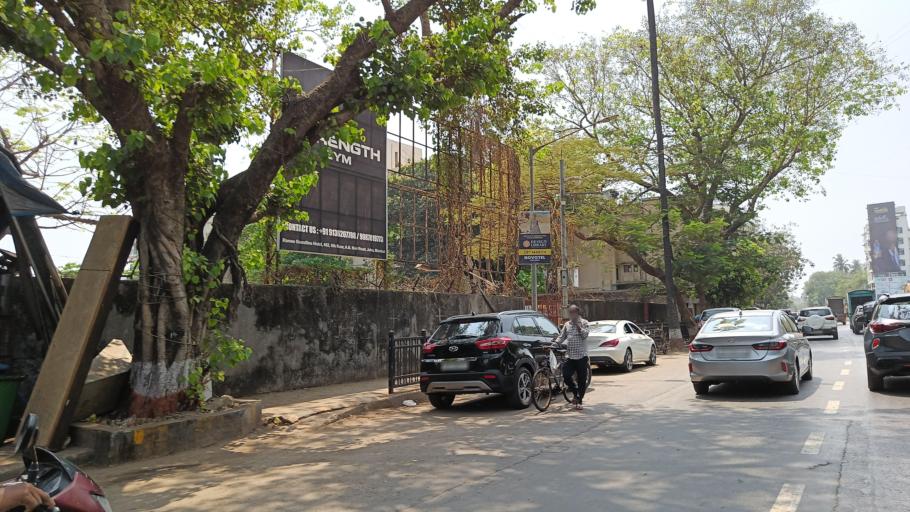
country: IN
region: Maharashtra
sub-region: Mumbai Suburban
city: Mumbai
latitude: 19.1032
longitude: 72.8269
